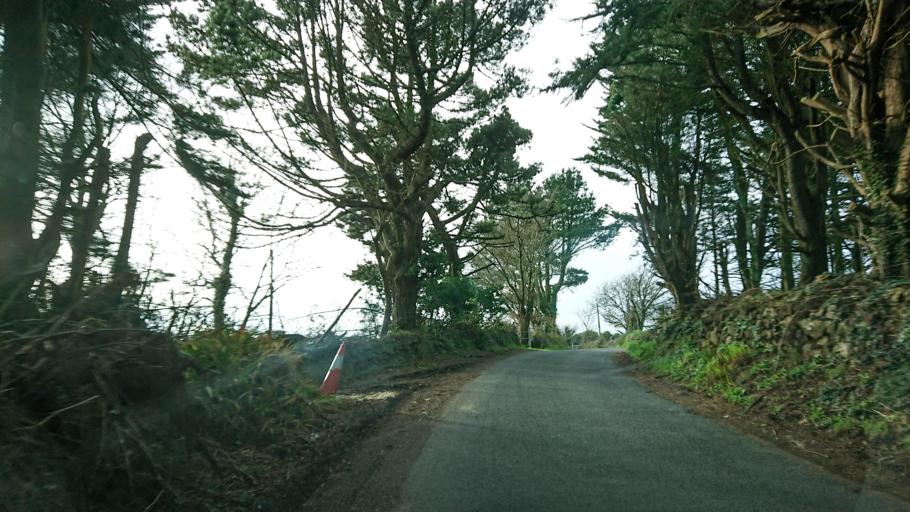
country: IE
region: Munster
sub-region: Waterford
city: Tra Mhor
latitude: 52.1755
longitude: -7.1748
